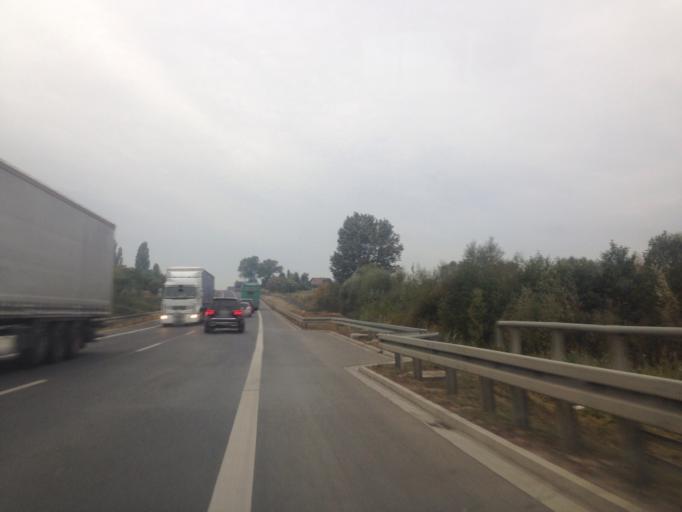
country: PL
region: Greater Poland Voivodeship
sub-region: Powiat gnieznienski
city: Niechanowo
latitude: 52.5554
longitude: 17.6910
